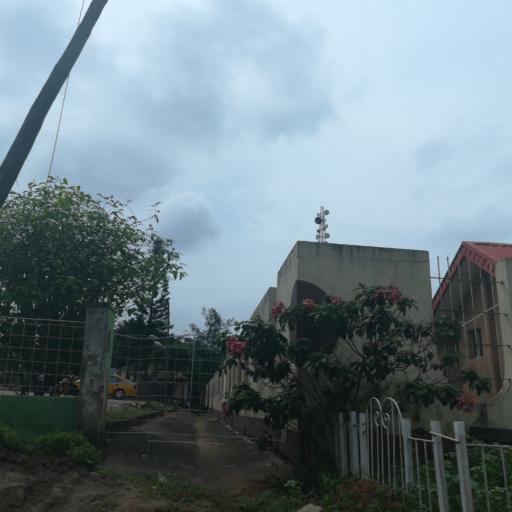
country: NG
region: Lagos
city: Ikeja
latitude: 6.6168
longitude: 3.3649
